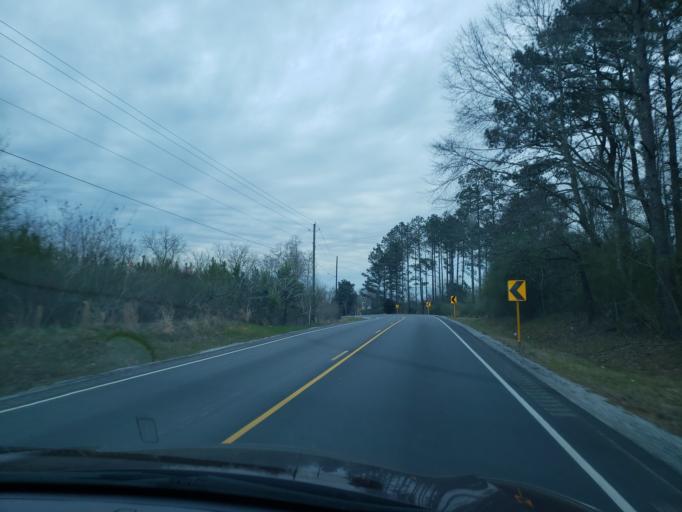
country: US
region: Alabama
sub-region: Randolph County
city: Roanoke
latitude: 33.0481
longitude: -85.3357
